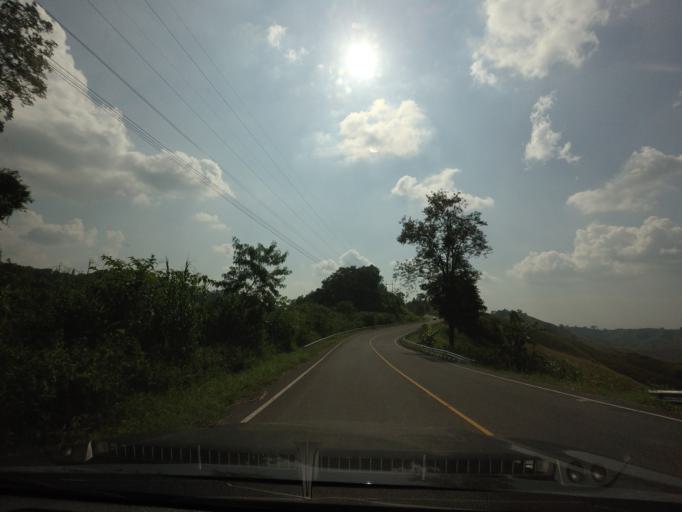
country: TH
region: Nan
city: Santi Suk
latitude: 18.9741
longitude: 100.9893
